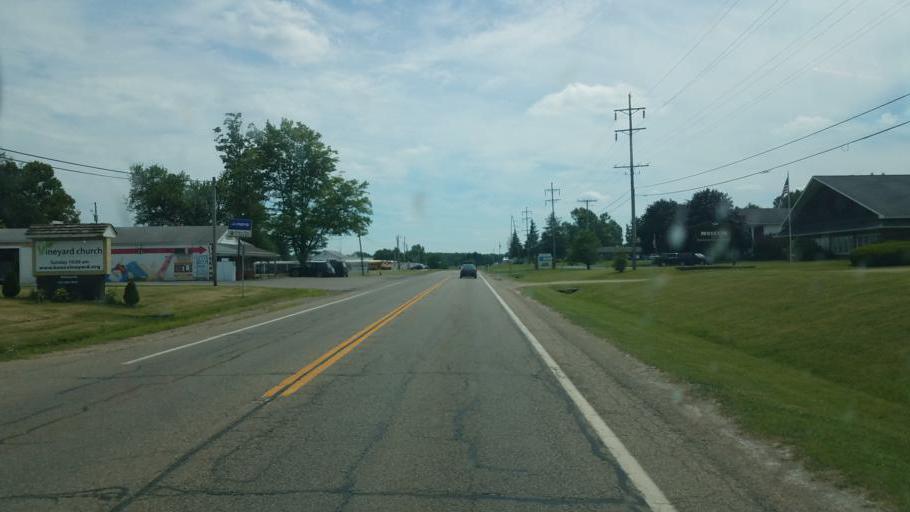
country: US
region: Ohio
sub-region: Knox County
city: Mount Vernon
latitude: 40.3798
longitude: -82.5080
